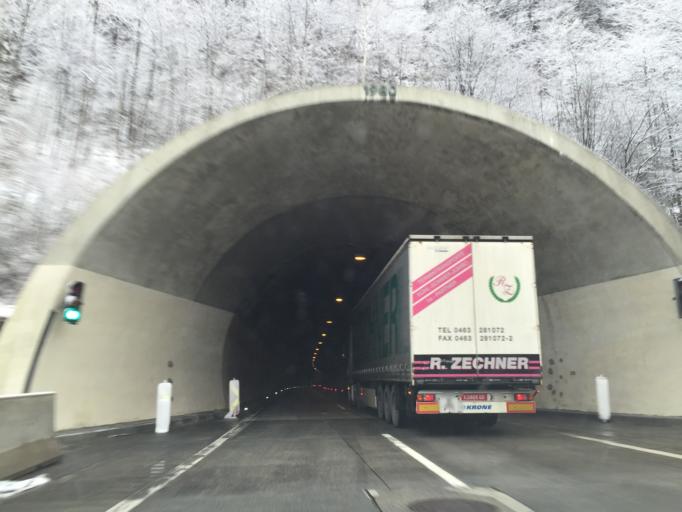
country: AT
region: Salzburg
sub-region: Politischer Bezirk Hallein
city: Golling an der Salzach
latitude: 47.5770
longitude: 13.1628
